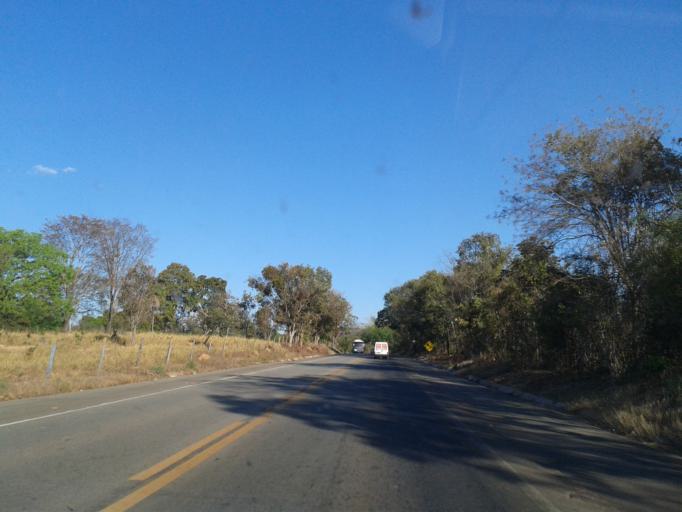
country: BR
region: Goias
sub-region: Itapuranga
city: Itapuranga
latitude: -15.4587
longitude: -50.3575
